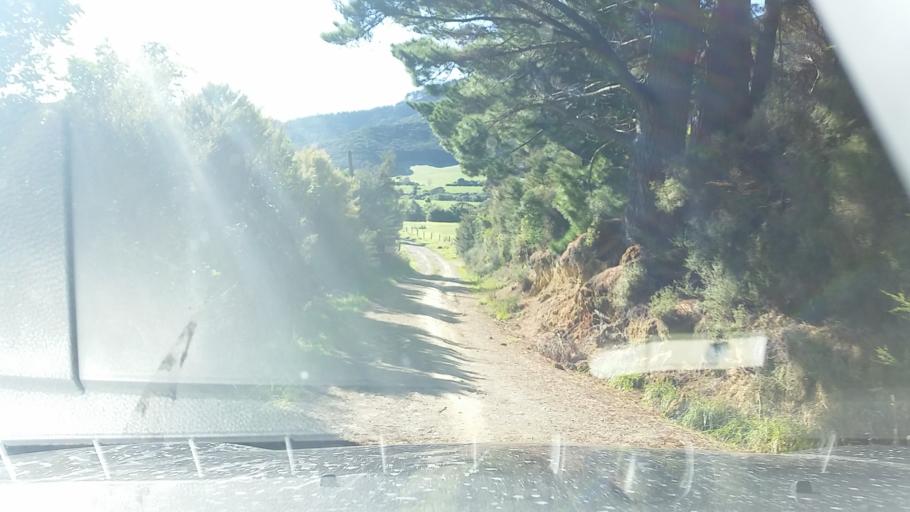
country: NZ
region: Marlborough
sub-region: Marlborough District
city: Picton
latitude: -41.1151
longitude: 173.9910
